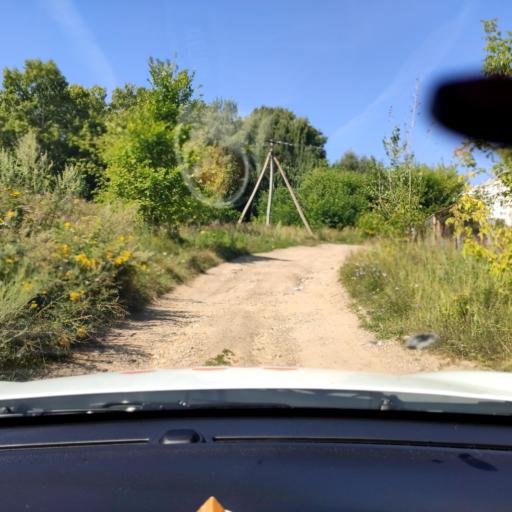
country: RU
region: Tatarstan
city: Stolbishchi
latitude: 55.7665
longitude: 49.2449
